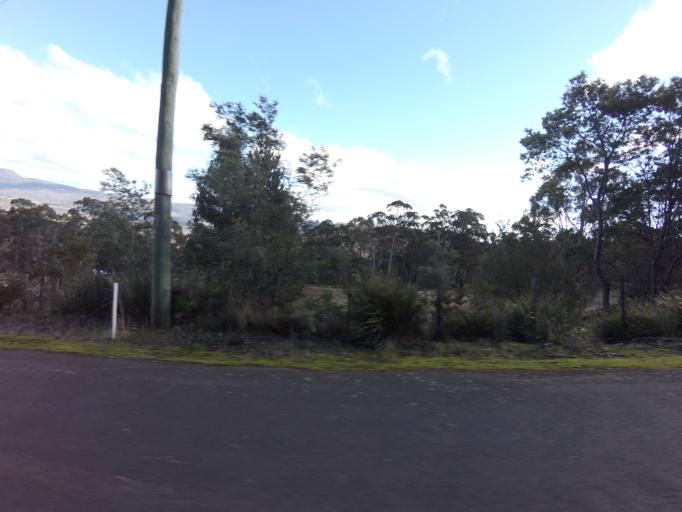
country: AU
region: Tasmania
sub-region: Derwent Valley
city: New Norfolk
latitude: -42.7315
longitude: 147.0331
